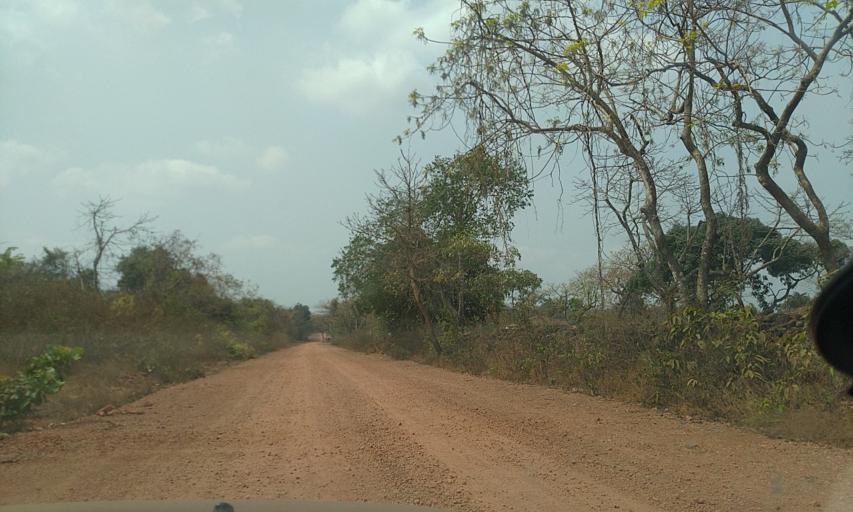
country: IN
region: Goa
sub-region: North Goa
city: Goa Velha
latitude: 15.4777
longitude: 73.9099
